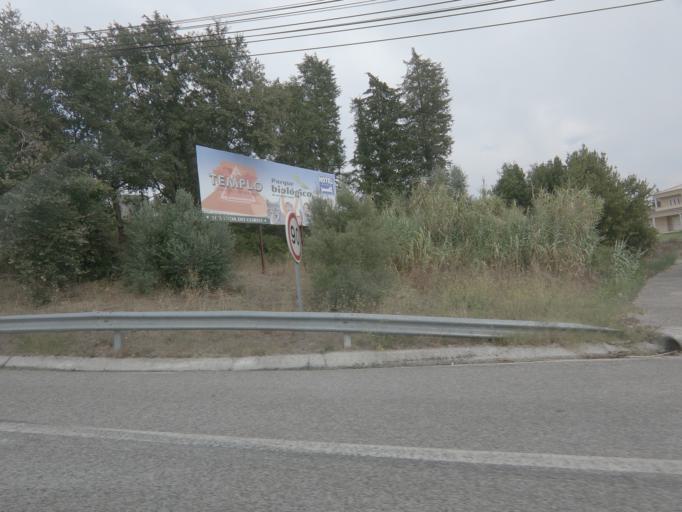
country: PT
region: Coimbra
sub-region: Condeixa-A-Nova
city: Condeixa-a-Nova
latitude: 40.1409
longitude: -8.4668
